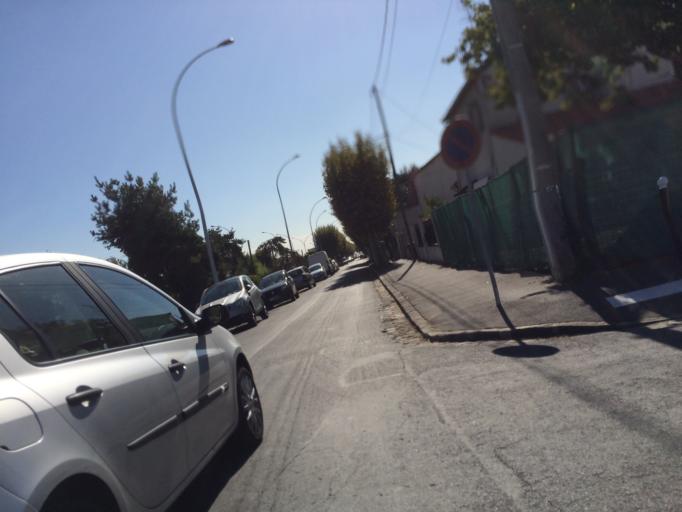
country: FR
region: Ile-de-France
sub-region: Departement de l'Essonne
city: Savigny-sur-Orge
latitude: 48.6931
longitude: 2.3561
